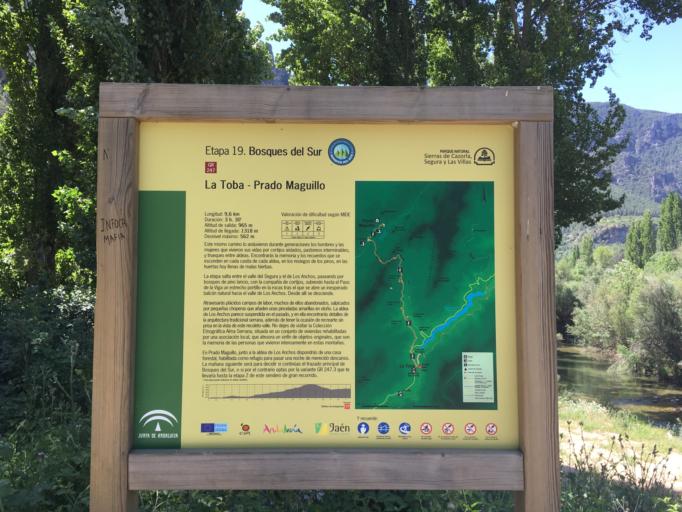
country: ES
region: Andalusia
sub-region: Provincia de Jaen
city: Segura de la Sierra
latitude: 38.1790
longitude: -2.5605
